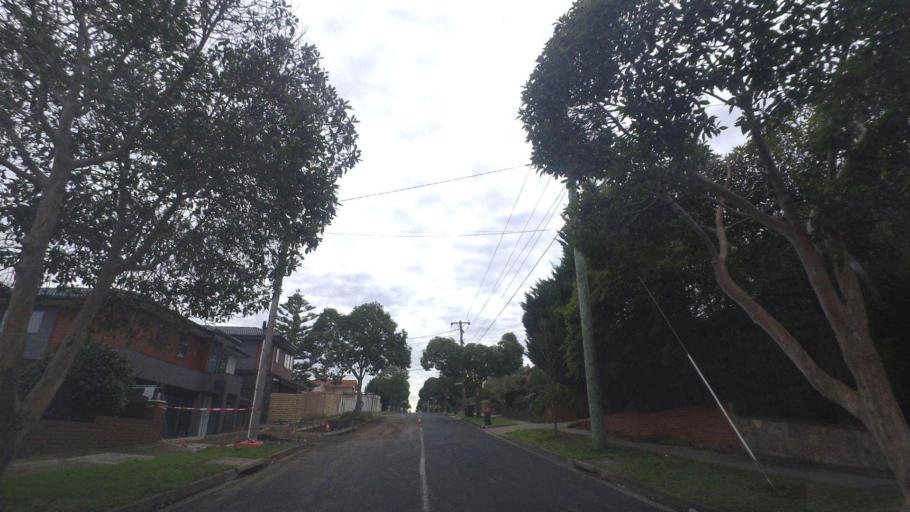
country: AU
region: Victoria
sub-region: Manningham
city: Templestowe Lower
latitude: -37.7656
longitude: 145.1047
